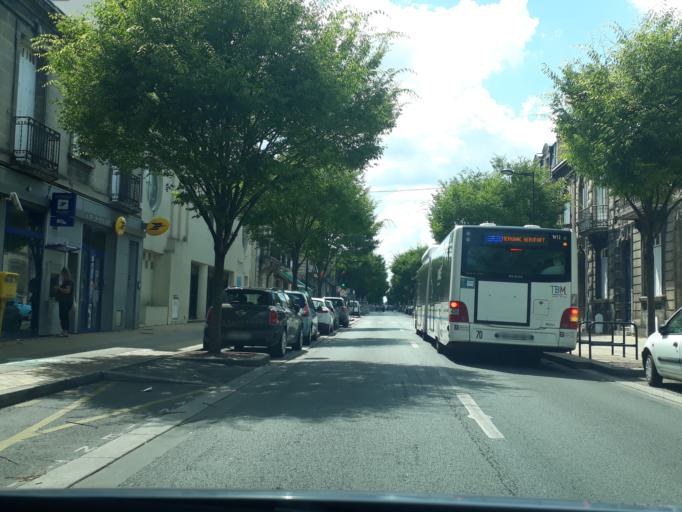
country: FR
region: Aquitaine
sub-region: Departement de la Gironde
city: Bordeaux
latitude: 44.8401
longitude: -0.5999
